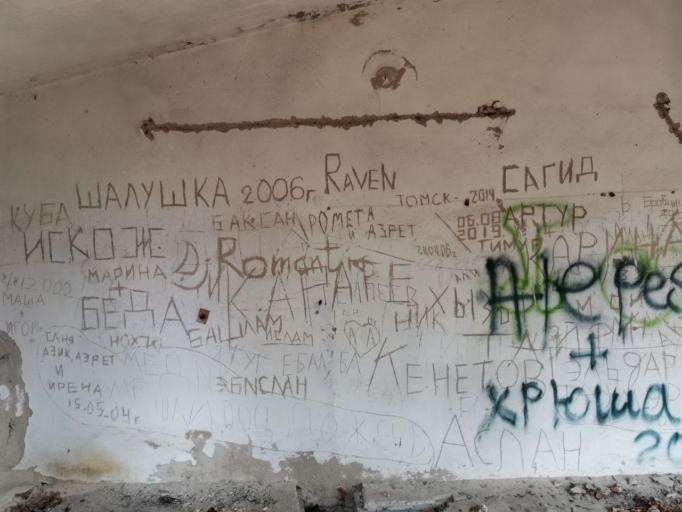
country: RU
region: Kabardino-Balkariya
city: Vol'nyy Aul
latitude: 43.4373
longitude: 43.5937
